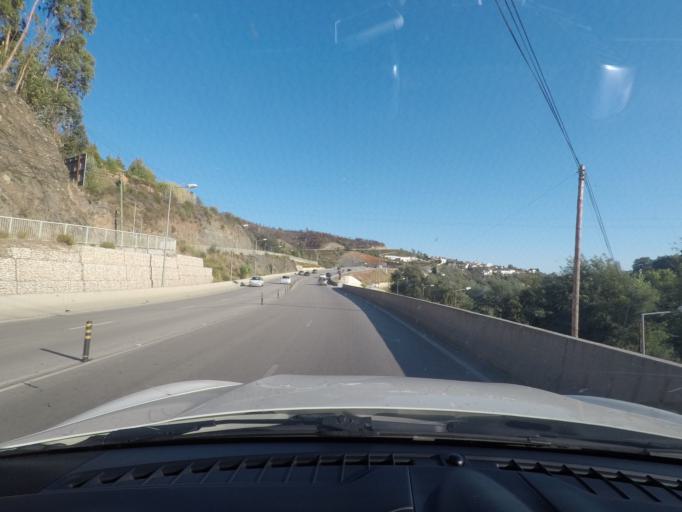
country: PT
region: Coimbra
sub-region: Coimbra
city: Coimbra
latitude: 40.1832
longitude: -8.3953
